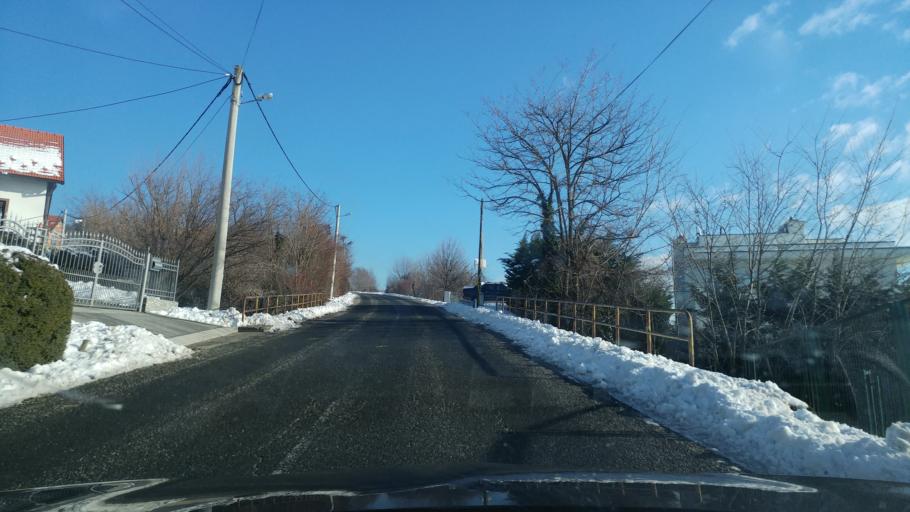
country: HR
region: Grad Zagreb
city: Stenjevec
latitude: 45.8354
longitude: 15.8799
